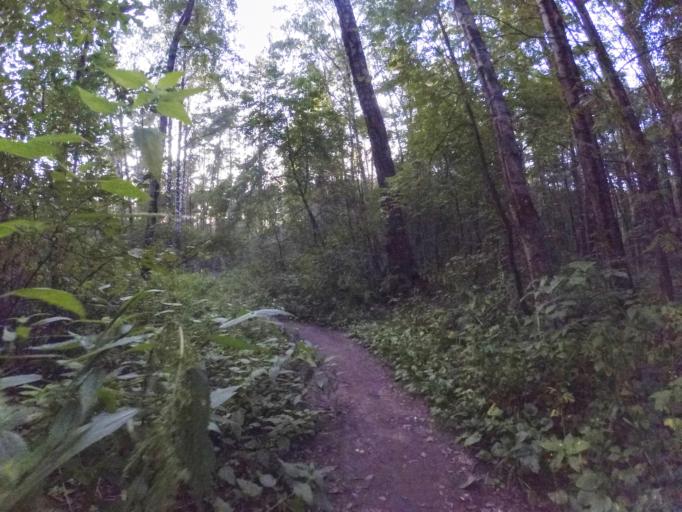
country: RU
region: Moscow
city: Khimki
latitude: 55.8734
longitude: 37.4289
